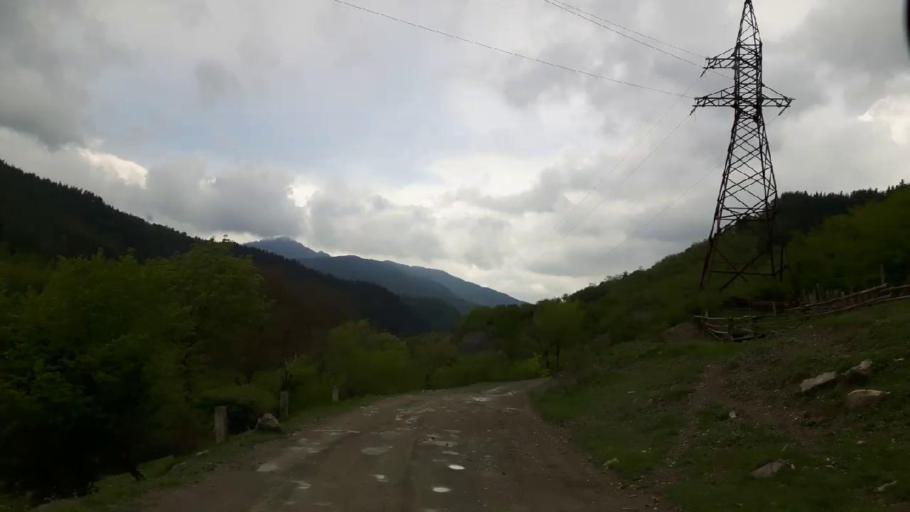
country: GE
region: Shida Kartli
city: Gori
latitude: 41.8649
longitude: 43.9760
